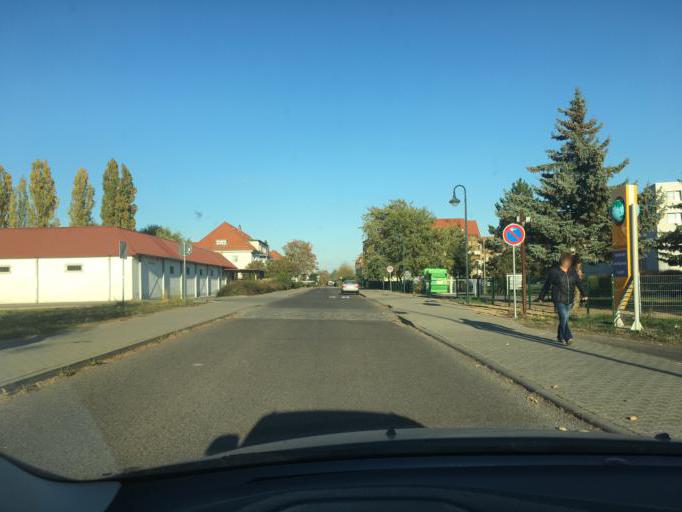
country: DE
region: Saxony
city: Markranstadt
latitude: 51.3076
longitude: 12.2293
